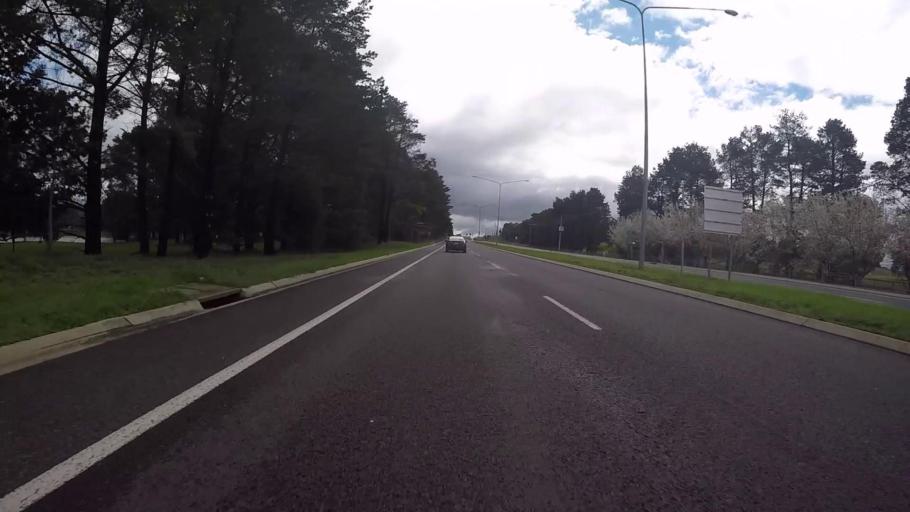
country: AU
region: Australian Capital Territory
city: Kaleen
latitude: -35.2370
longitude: 149.1324
